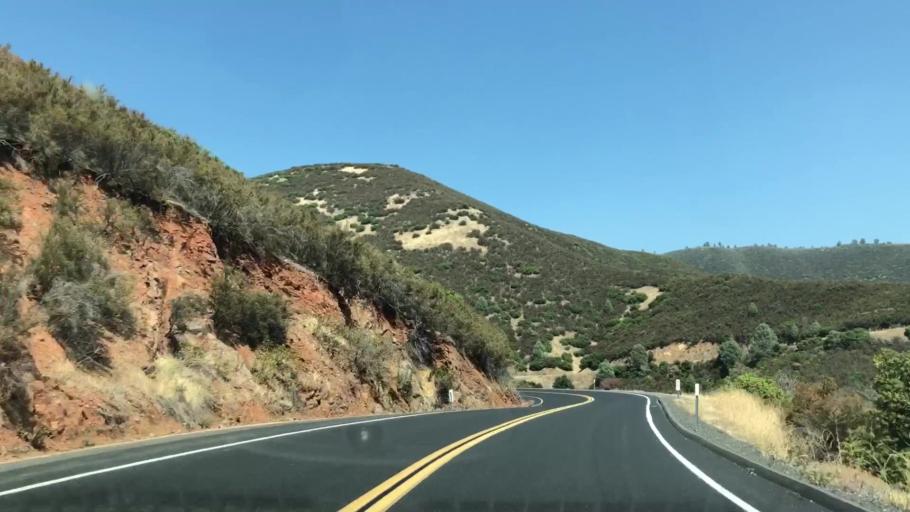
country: US
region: California
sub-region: Tuolumne County
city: Tuolumne City
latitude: 37.8189
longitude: -120.2946
